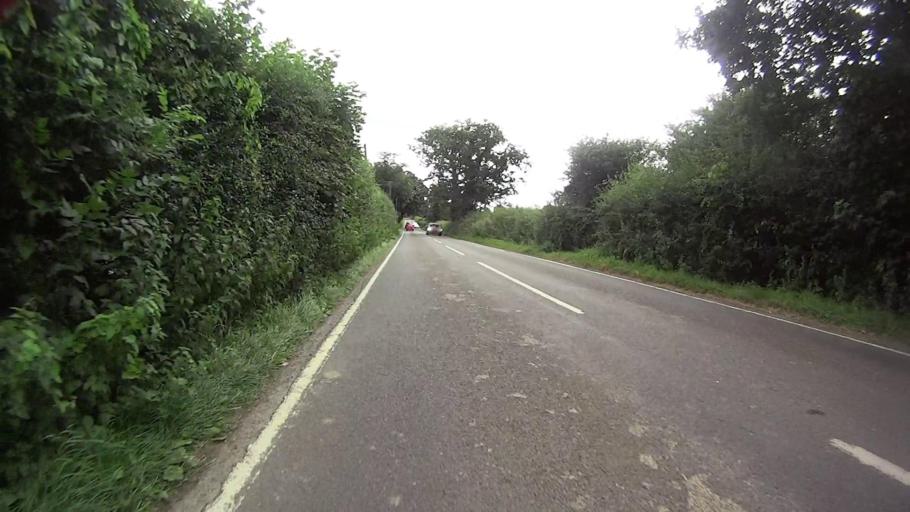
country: GB
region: England
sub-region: Surrey
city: Reigate
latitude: 51.1833
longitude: -0.2319
